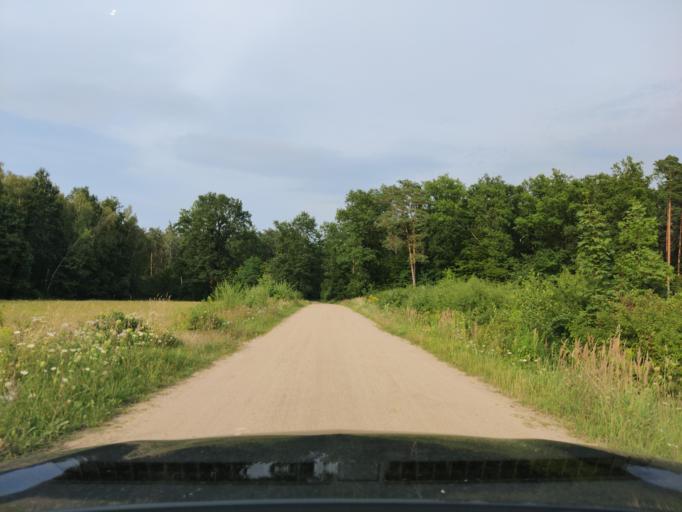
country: PL
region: Masovian Voivodeship
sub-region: Powiat pultuski
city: Obryte
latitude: 52.6992
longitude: 21.2085
